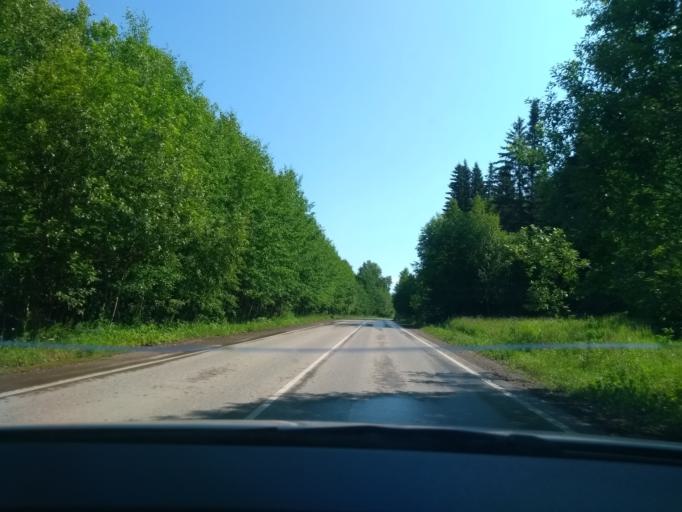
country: RU
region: Perm
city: Bershet'
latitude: 57.8170
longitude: 56.4880
